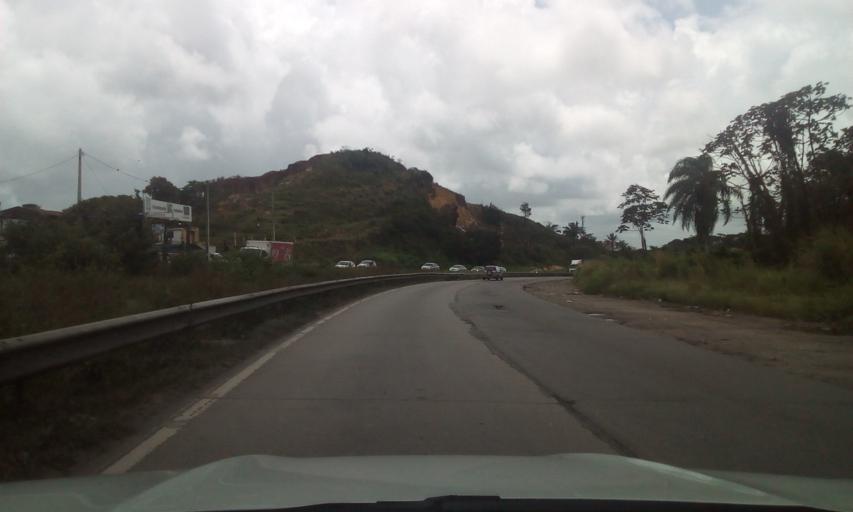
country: BR
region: Pernambuco
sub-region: Jaboatao Dos Guararapes
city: Jaboatao dos Guararapes
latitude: -8.1062
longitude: -34.9486
